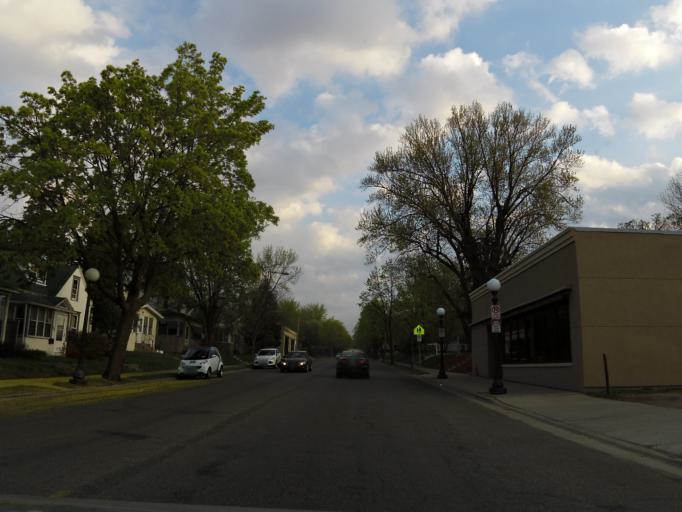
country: US
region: Minnesota
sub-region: Dakota County
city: West Saint Paul
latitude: 44.9265
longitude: -93.1019
